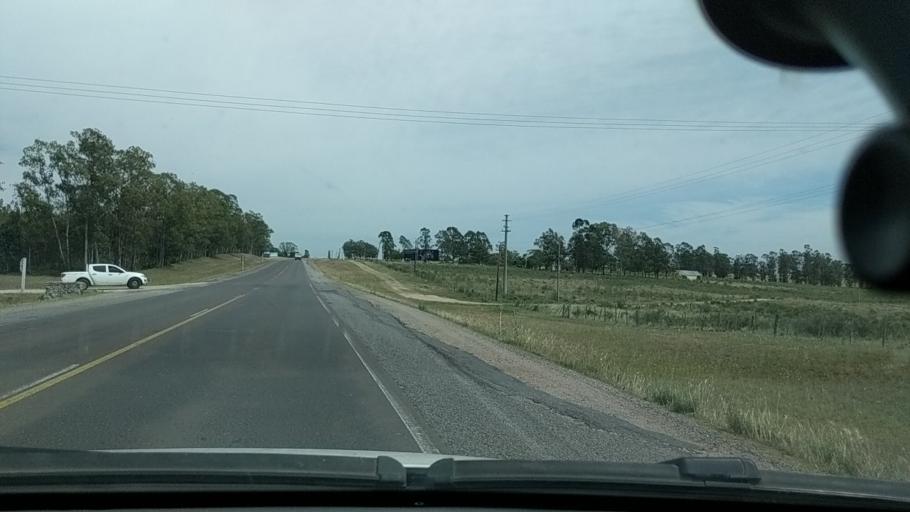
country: UY
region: Durazno
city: Durazno
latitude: -33.4366
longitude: -56.4882
